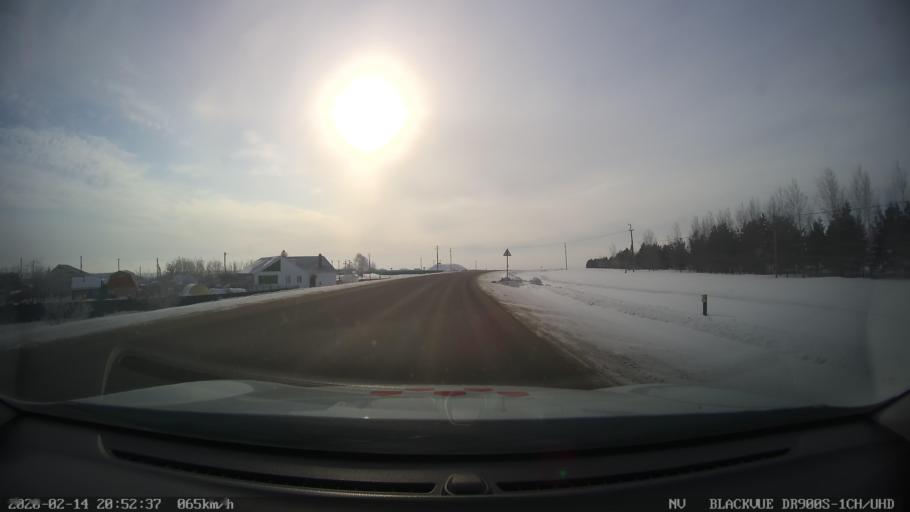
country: RU
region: Tatarstan
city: Kuybyshevskiy Zaton
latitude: 55.2025
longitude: 49.2497
